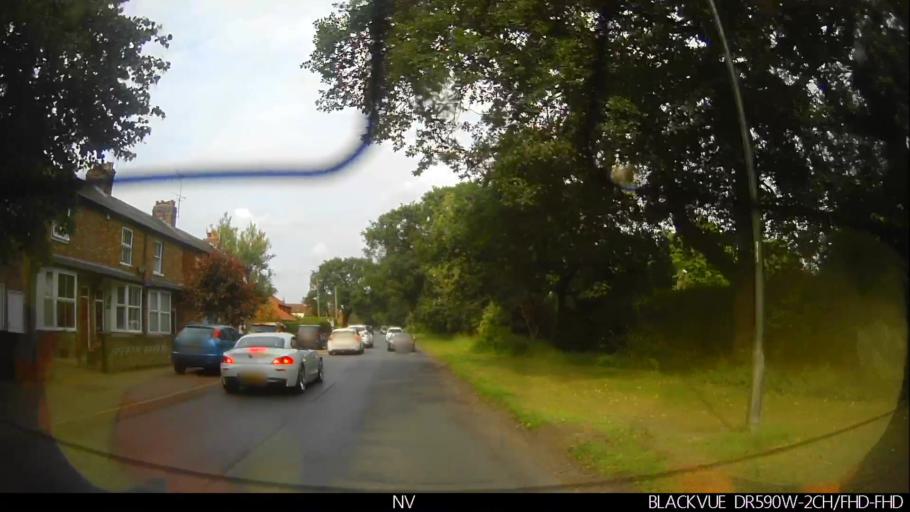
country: GB
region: England
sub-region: North Yorkshire
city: Strensall
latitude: 54.0287
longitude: -1.0388
